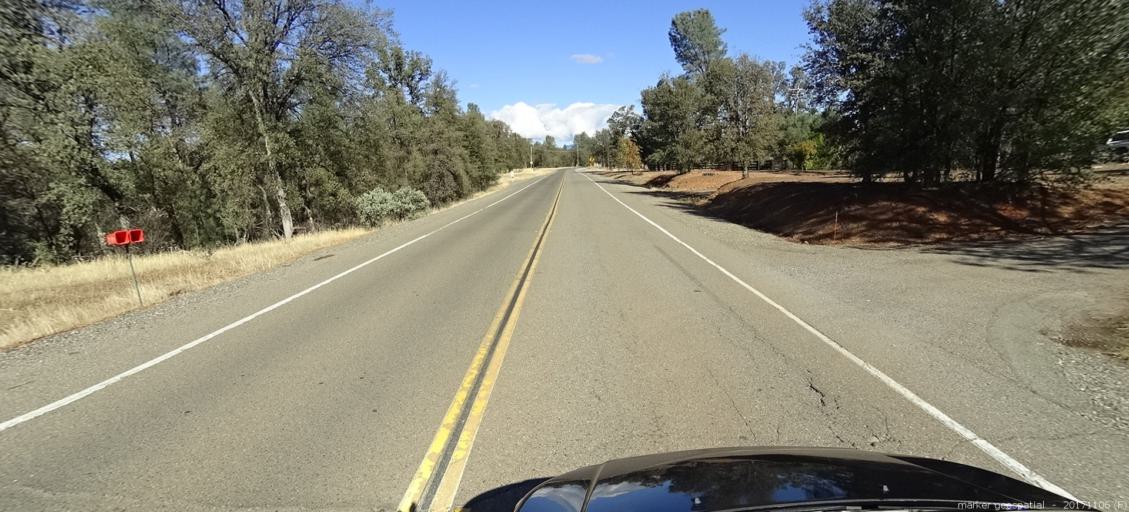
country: US
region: California
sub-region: Shasta County
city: Palo Cedro
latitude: 40.5968
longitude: -122.2861
